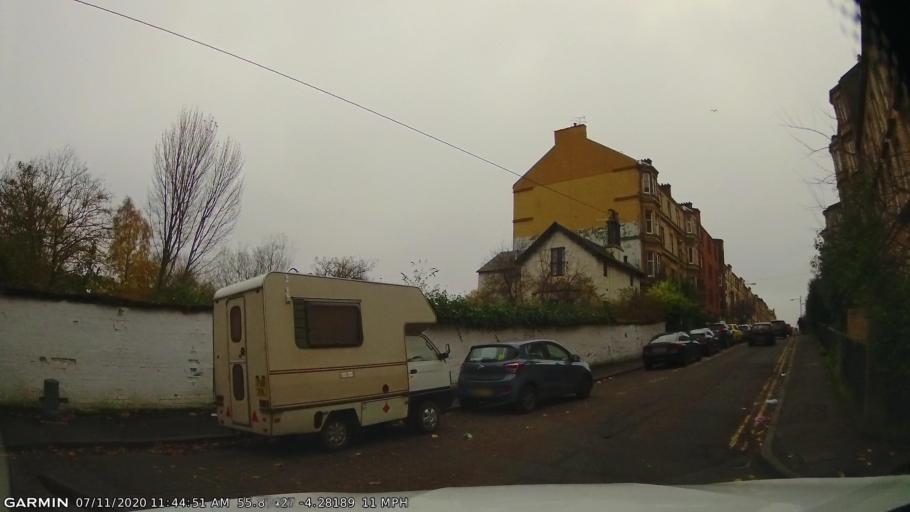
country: GB
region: Scotland
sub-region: Glasgow City
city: Glasgow
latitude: 55.8745
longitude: -4.2816
